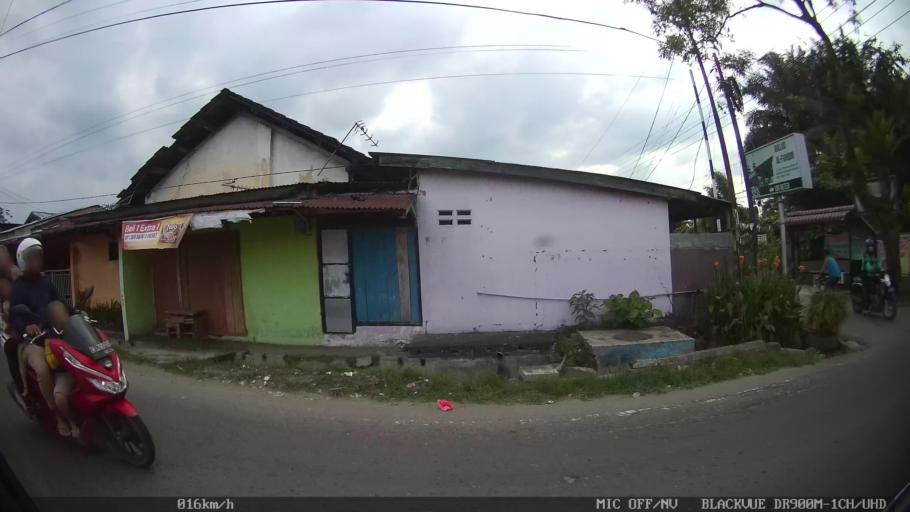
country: ID
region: North Sumatra
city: Deli Tua
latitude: 3.5450
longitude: 98.6798
